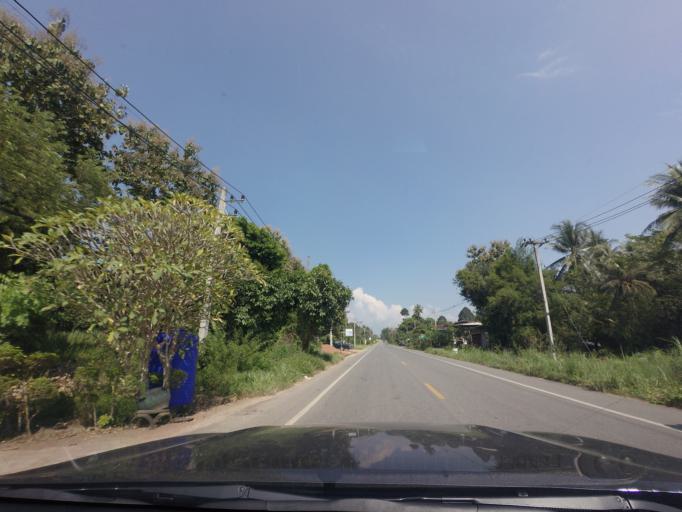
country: TH
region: Phitsanulok
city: Nakhon Thai
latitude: 17.1100
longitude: 100.8150
